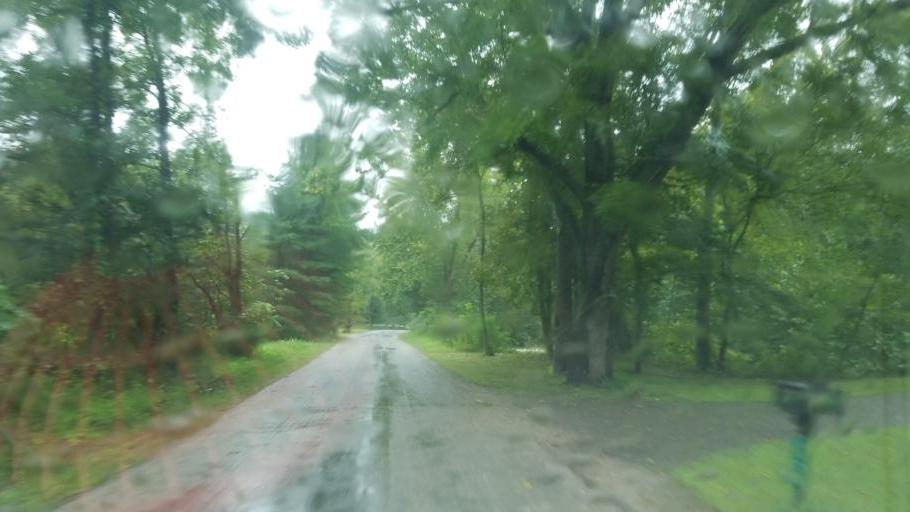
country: US
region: Ohio
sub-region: Adams County
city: Peebles
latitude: 38.8112
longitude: -83.2427
